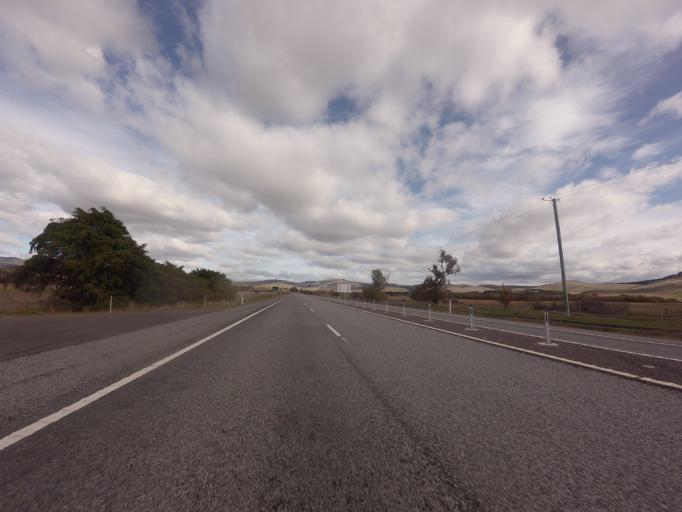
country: AU
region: Tasmania
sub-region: Brighton
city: Bridgewater
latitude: -42.4743
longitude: 147.1810
